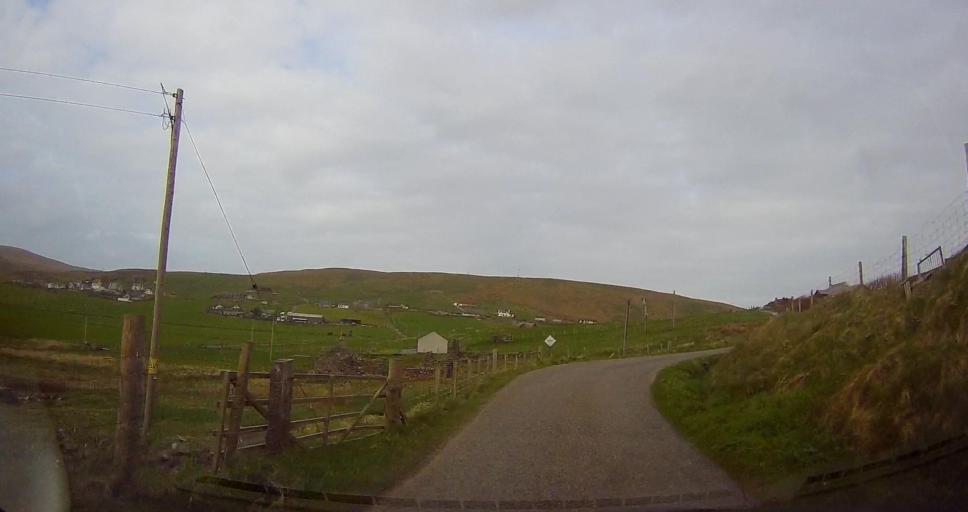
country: GB
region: Scotland
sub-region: Shetland Islands
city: Sandwick
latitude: 60.0478
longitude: -1.2160
